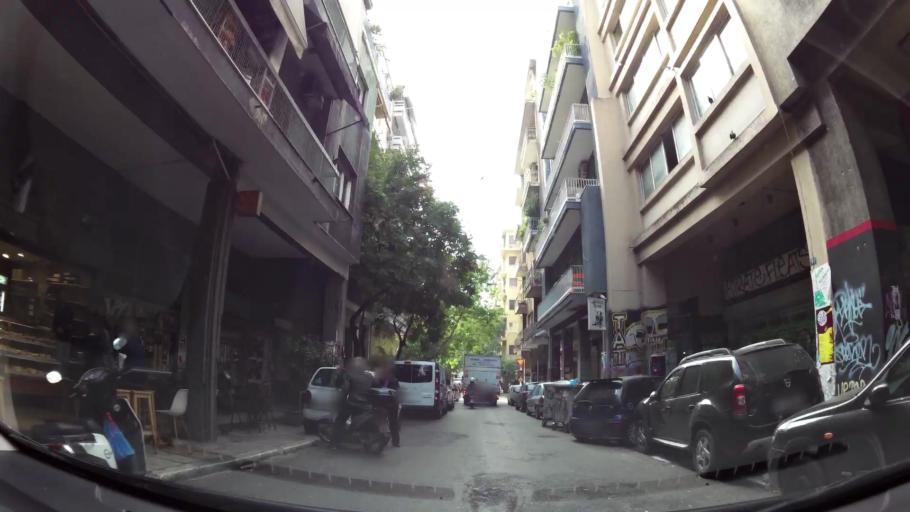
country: GR
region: Attica
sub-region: Nomarchia Athinas
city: Kipseli
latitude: 37.9873
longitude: 23.7348
